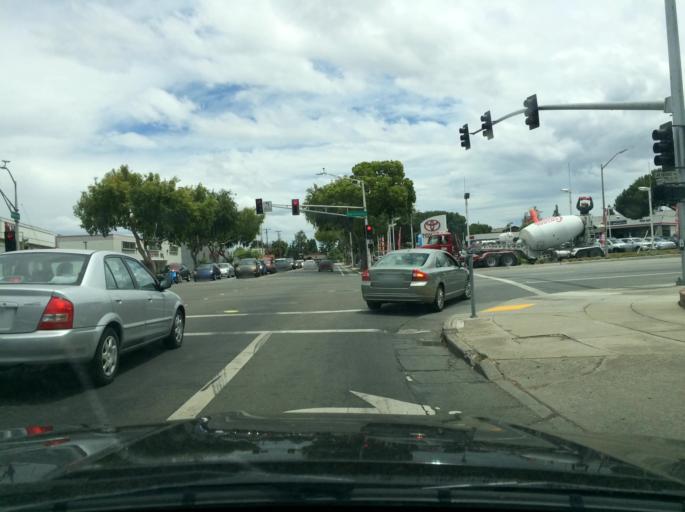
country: US
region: California
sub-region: Santa Clara County
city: Los Altos
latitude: 37.4163
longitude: -122.1038
